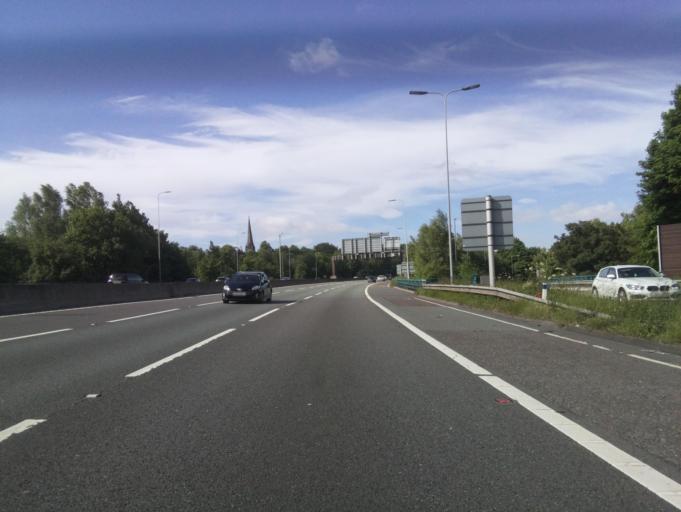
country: GB
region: England
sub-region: City and Borough of Salford
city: Walkden
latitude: 53.4986
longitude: -2.3845
